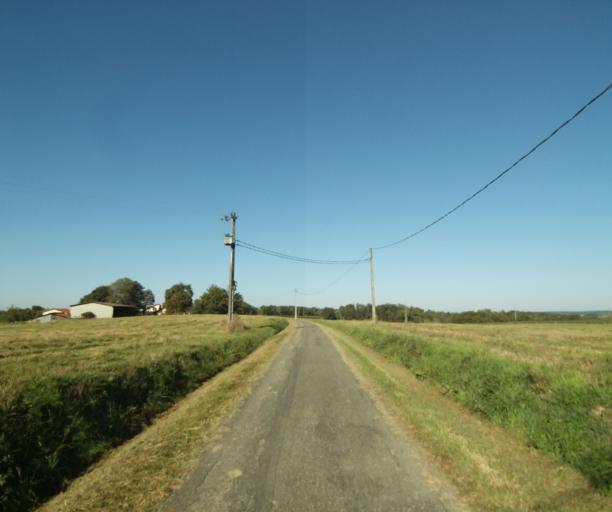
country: FR
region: Midi-Pyrenees
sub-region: Departement du Gers
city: Cazaubon
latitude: 43.9159
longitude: -0.0022
